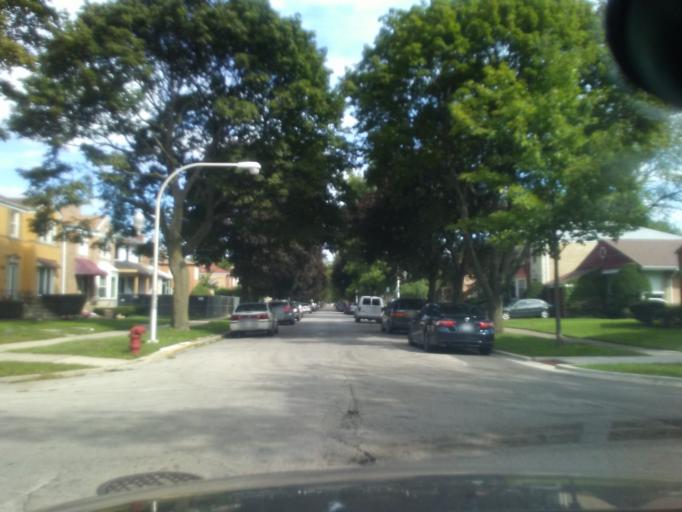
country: US
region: Illinois
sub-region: Cook County
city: Lincolnwood
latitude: 42.0030
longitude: -87.7022
